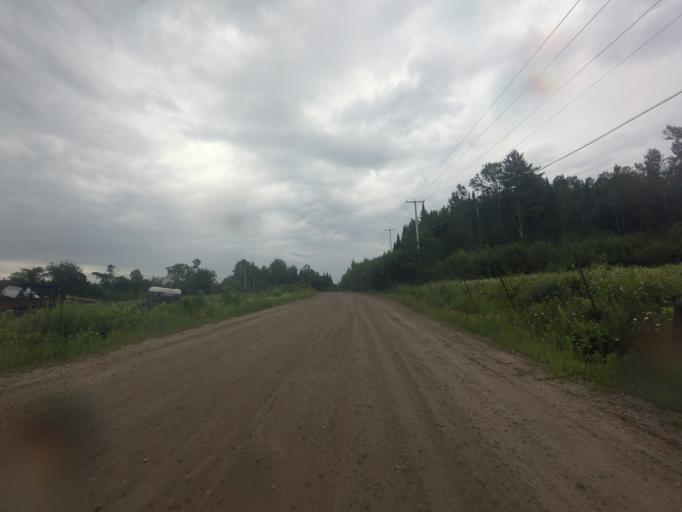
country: CA
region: Quebec
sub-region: Outaouais
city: Maniwaki
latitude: 46.4482
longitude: -75.9383
